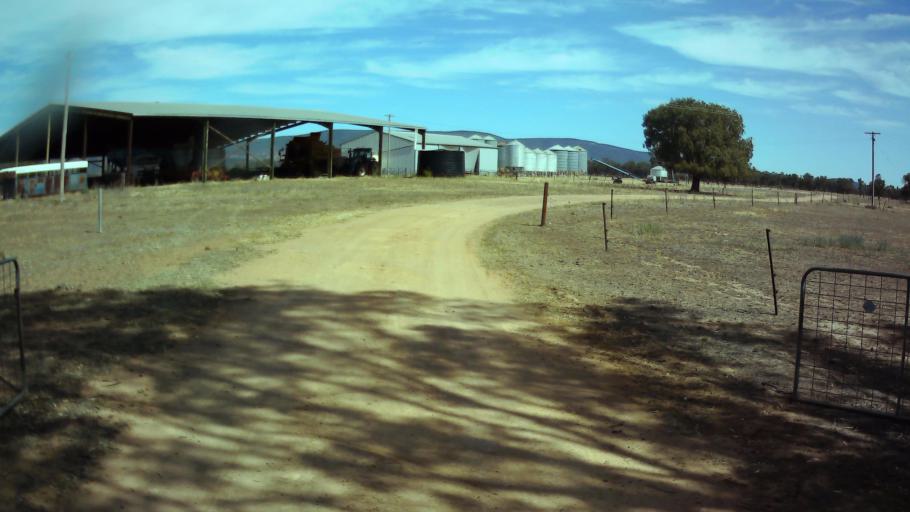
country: AU
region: New South Wales
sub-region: Weddin
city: Grenfell
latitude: -33.6756
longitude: 148.2892
